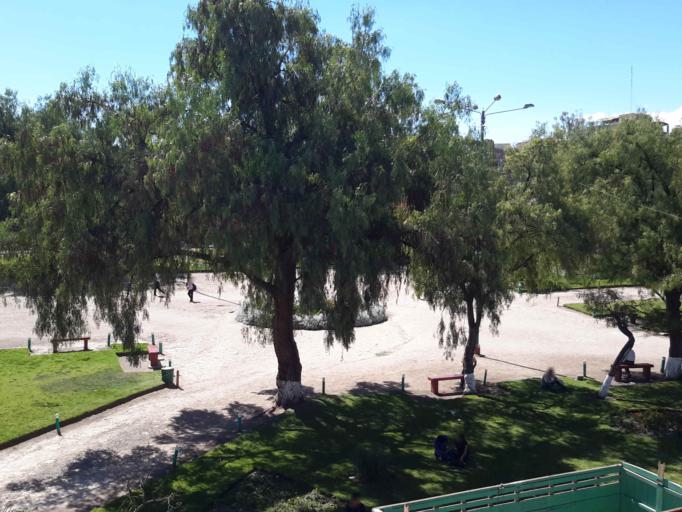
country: PE
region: Ayacucho
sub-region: Provincia de Huamanga
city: Ayacucho
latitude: -13.1558
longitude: -74.2179
